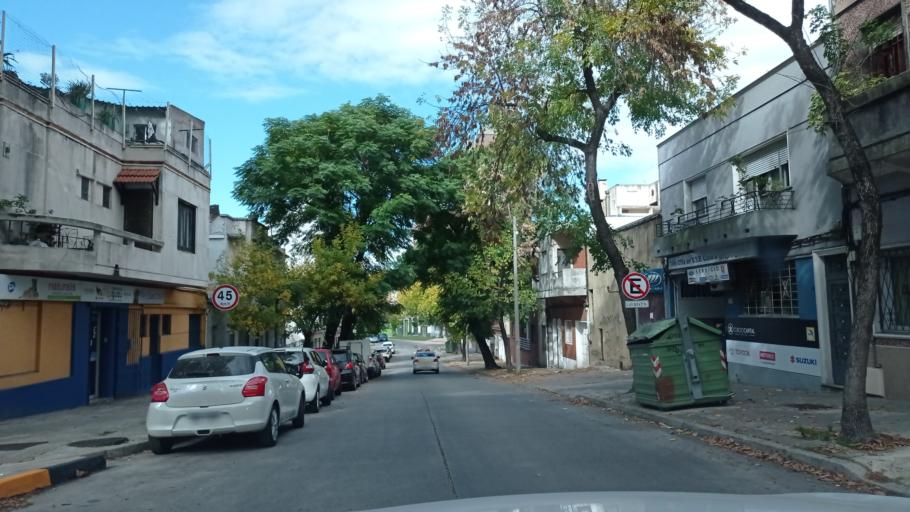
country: UY
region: Montevideo
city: Montevideo
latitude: -34.9048
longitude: -56.1526
